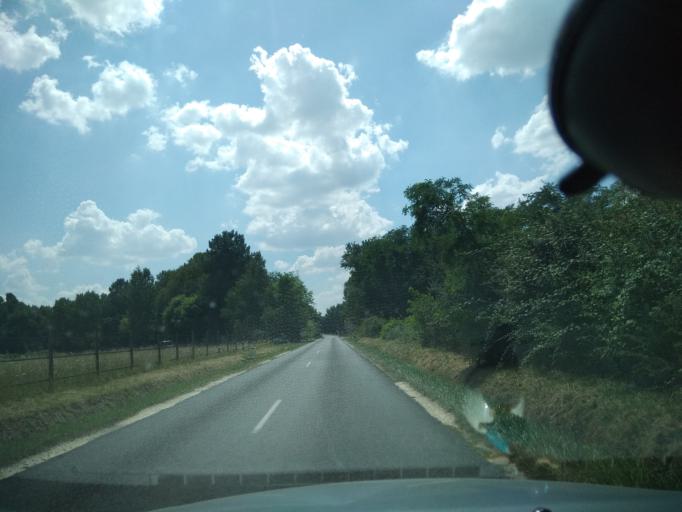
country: FR
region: Centre
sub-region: Departement d'Indre-et-Loire
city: Civray-de-Touraine
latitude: 47.3282
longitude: 1.0424
